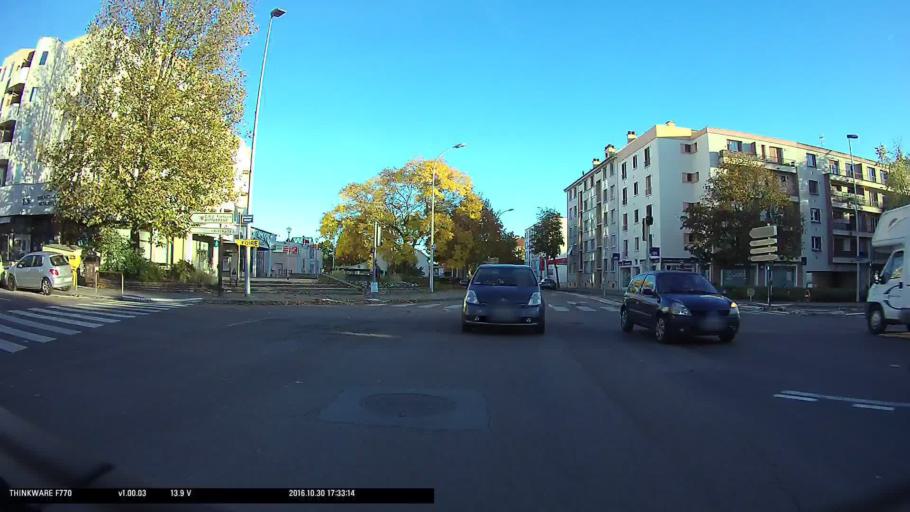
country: FR
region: Bourgogne
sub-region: Departement de la Cote-d'Or
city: Longvic
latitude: 47.3079
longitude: 5.0569
